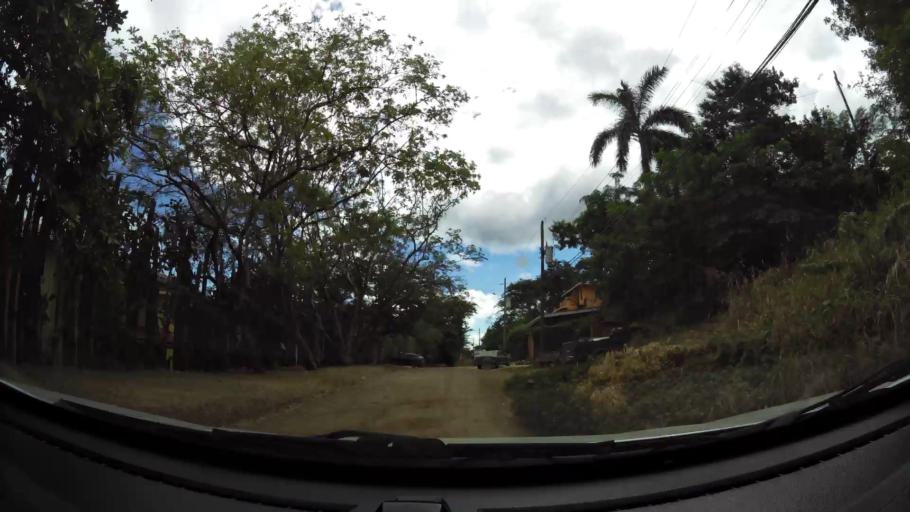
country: CR
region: Guanacaste
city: Santa Cruz
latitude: 10.2955
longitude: -85.8391
